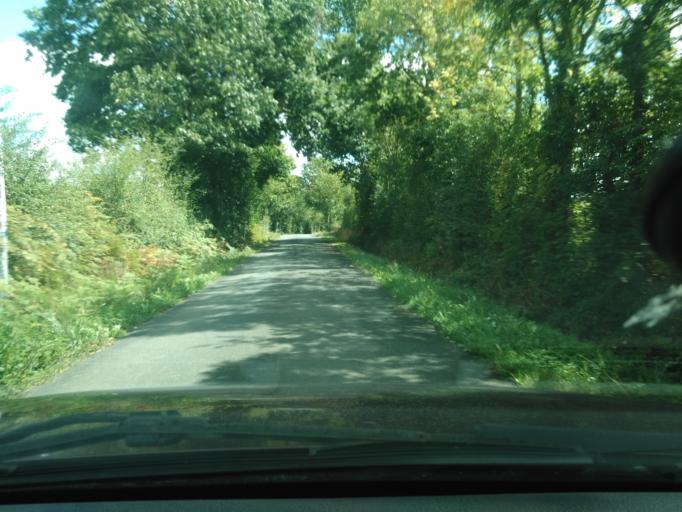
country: FR
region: Pays de la Loire
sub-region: Departement de la Vendee
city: Dompierre-sur-Yon
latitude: 46.7430
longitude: -1.3613
